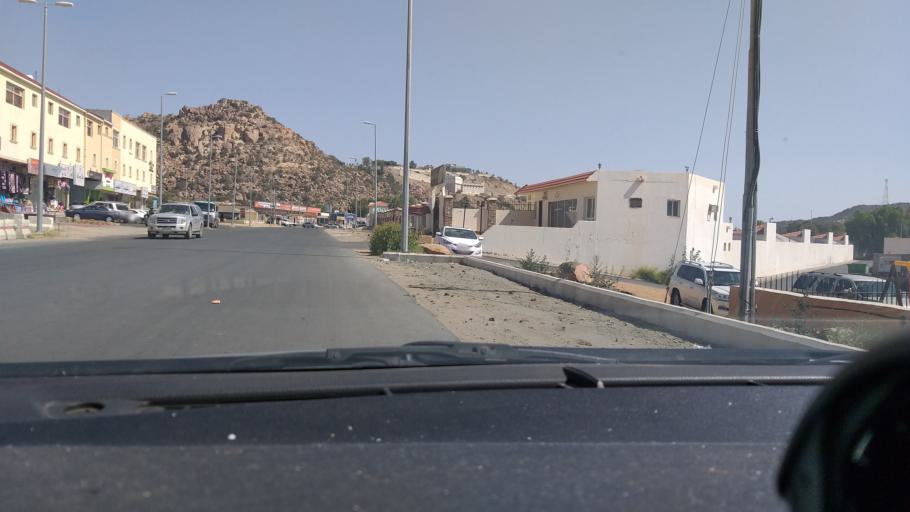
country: SA
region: Makkah
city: Ash Shafa
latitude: 21.0673
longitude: 40.3090
